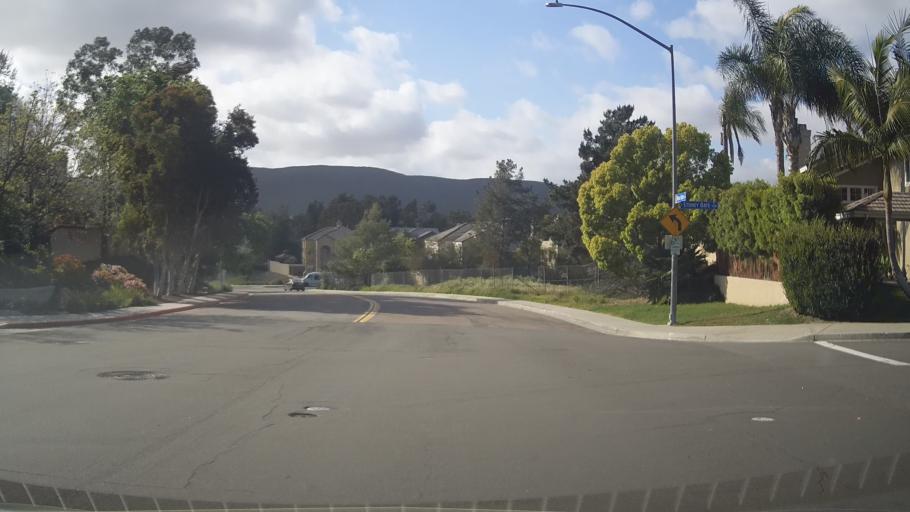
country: US
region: California
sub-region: San Diego County
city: Poway
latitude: 32.9702
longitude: -117.0820
